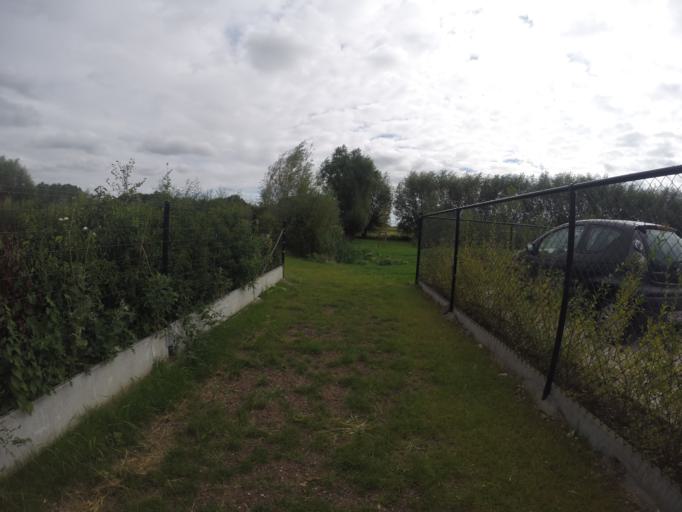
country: BE
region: Flanders
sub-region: Provincie Oost-Vlaanderen
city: Aalter
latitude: 51.0967
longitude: 3.4531
